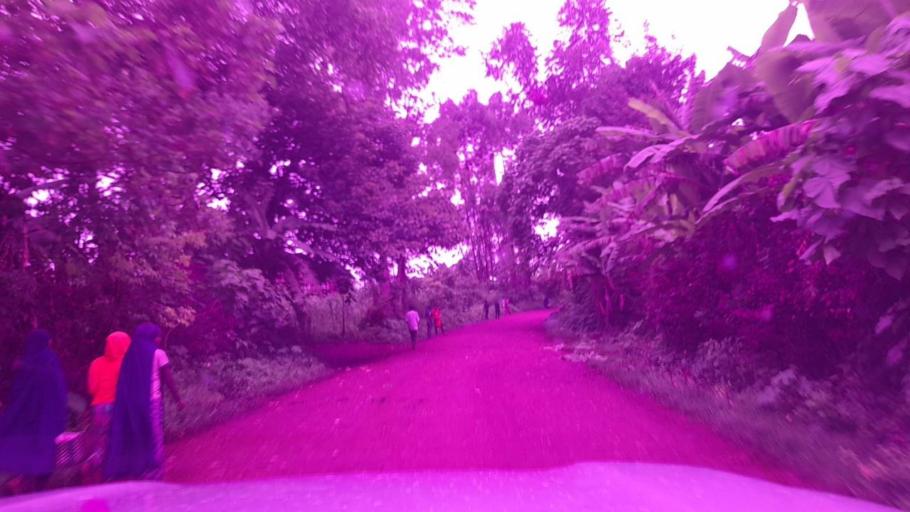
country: ET
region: Southern Nations, Nationalities, and People's Region
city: Bonga
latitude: 7.5848
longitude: 36.0166
